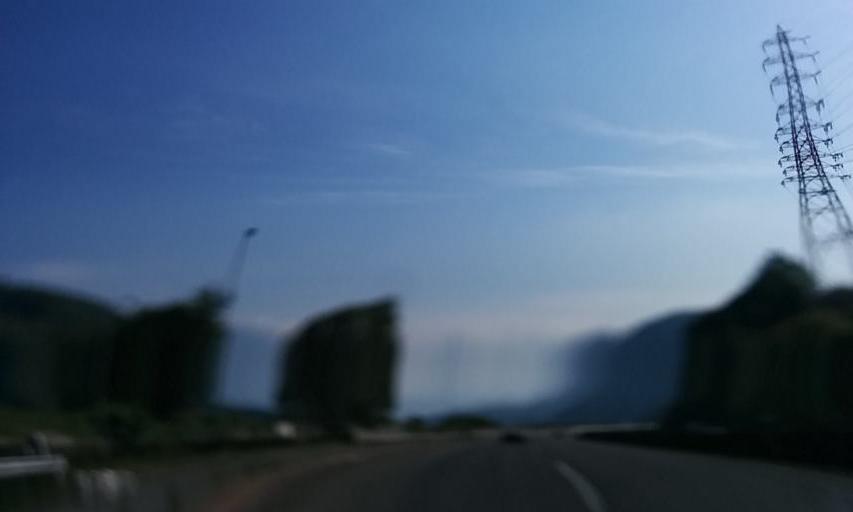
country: JP
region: Shiga Prefecture
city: Nagahama
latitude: 35.3221
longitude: 136.3383
